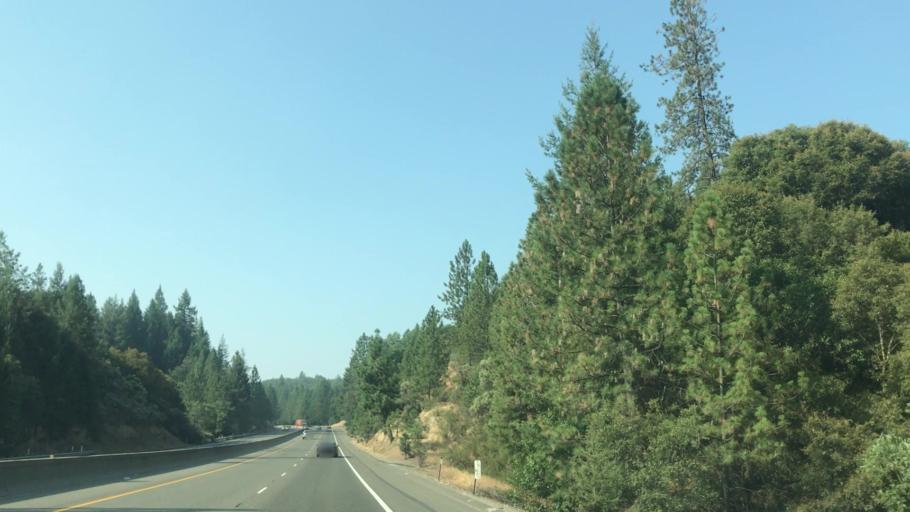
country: US
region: California
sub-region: Placer County
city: Colfax
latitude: 39.0752
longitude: -120.9618
